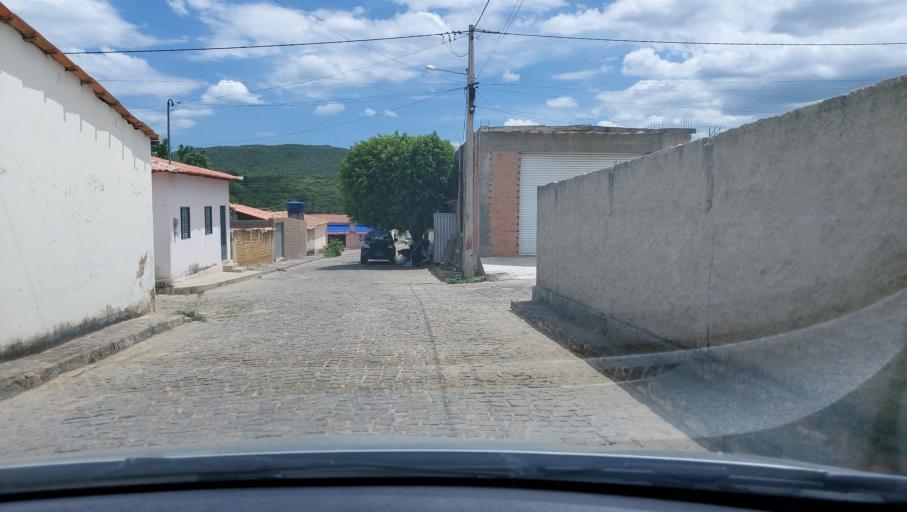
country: BR
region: Bahia
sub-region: Oliveira Dos Brejinhos
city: Beira Rio
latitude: -11.9979
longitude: -42.6290
